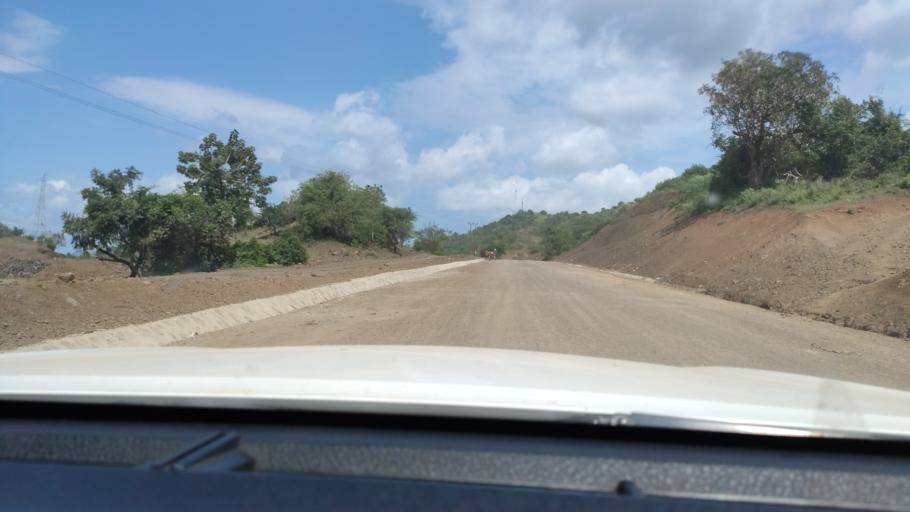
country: ET
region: Southern Nations, Nationalities, and People's Region
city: Felege Neway
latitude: 6.3902
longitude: 37.0636
